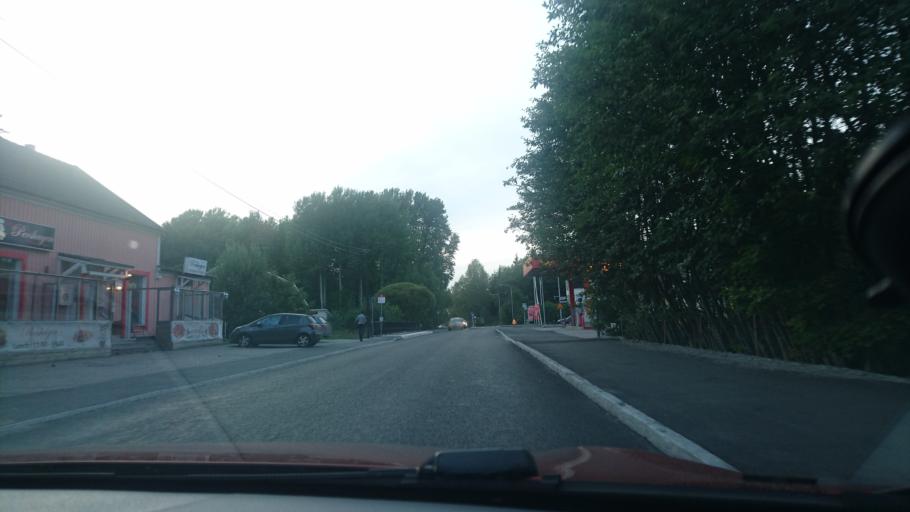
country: SE
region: Stockholm
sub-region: Sodertalje Kommun
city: Pershagen
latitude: 59.1544
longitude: 17.6477
